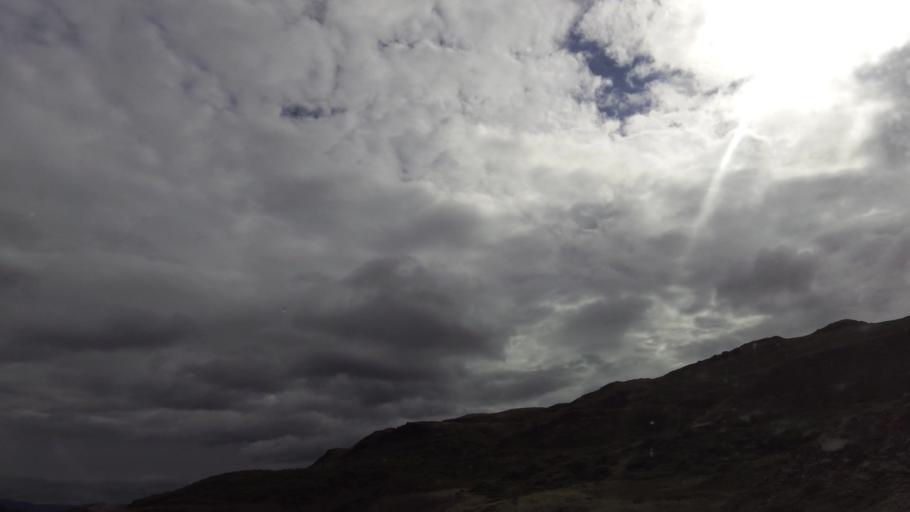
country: IS
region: West
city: Stykkisholmur
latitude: 65.5239
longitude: -22.1215
